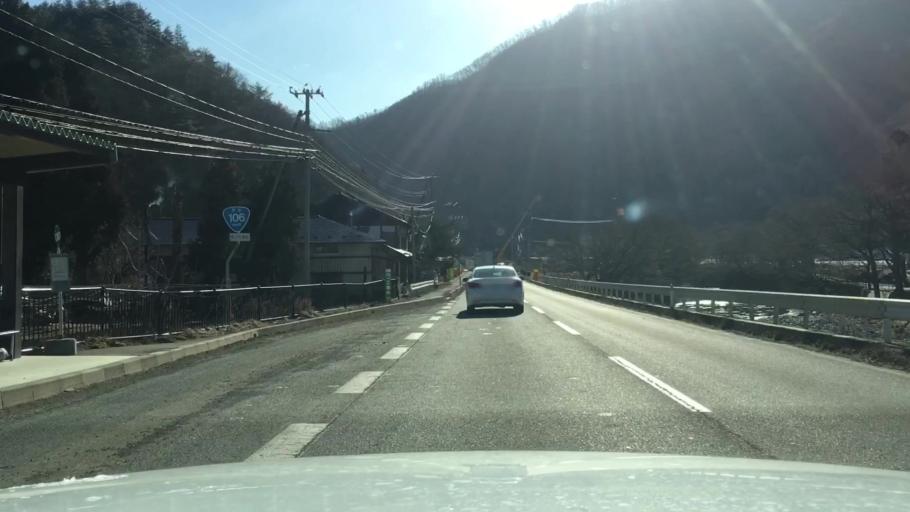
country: JP
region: Iwate
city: Tono
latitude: 39.6137
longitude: 141.6286
